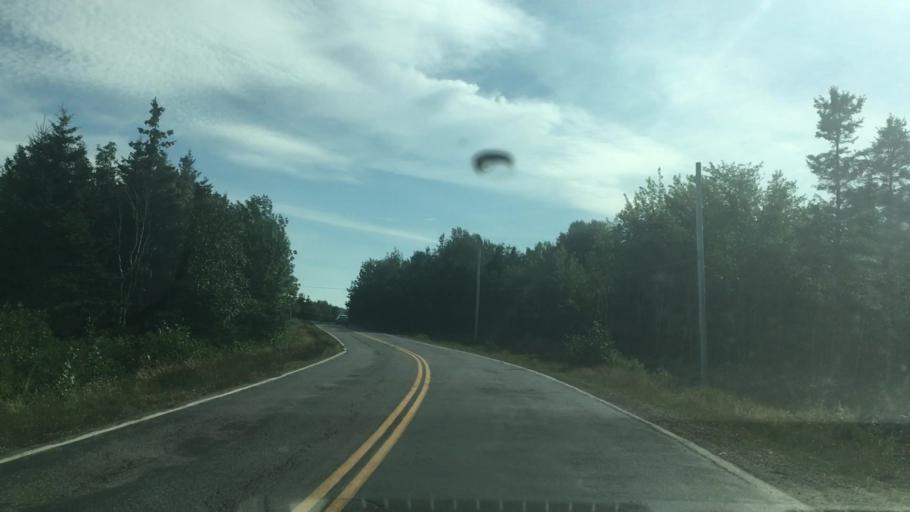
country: CA
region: Nova Scotia
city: Sydney Mines
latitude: 46.8807
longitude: -60.5158
